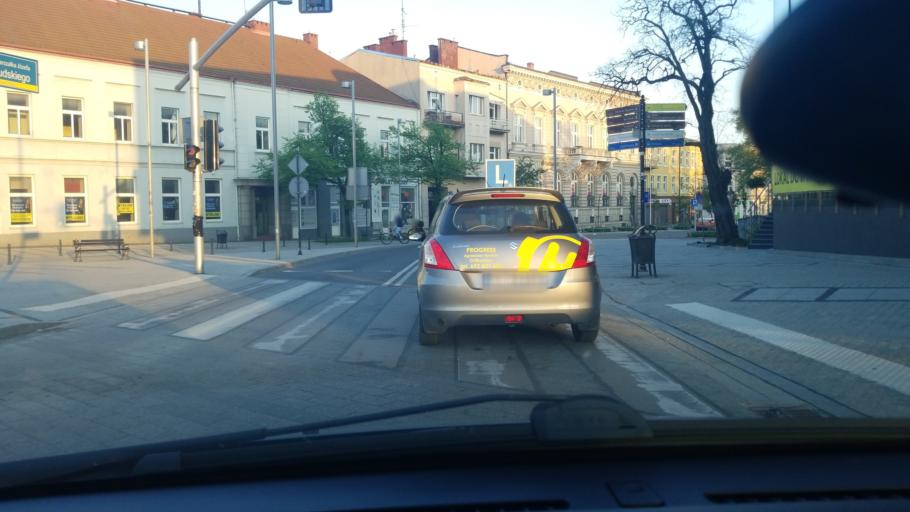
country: PL
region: Silesian Voivodeship
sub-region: Czestochowa
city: Czestochowa
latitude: 50.8118
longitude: 19.1220
